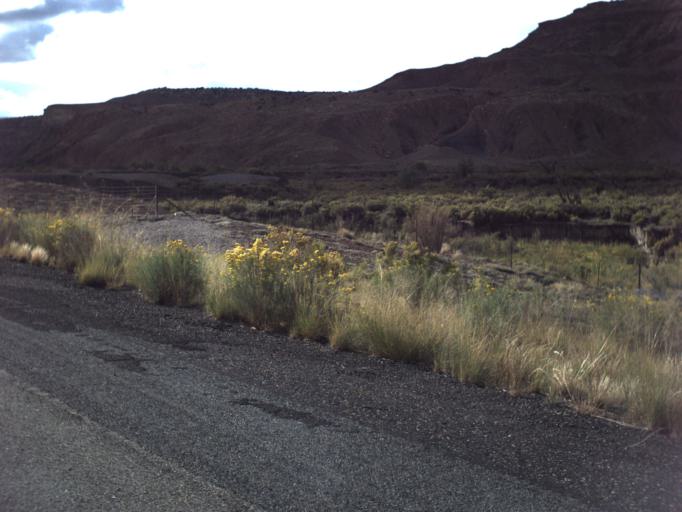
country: US
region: Utah
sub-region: Emery County
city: Ferron
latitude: 38.8110
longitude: -111.2162
